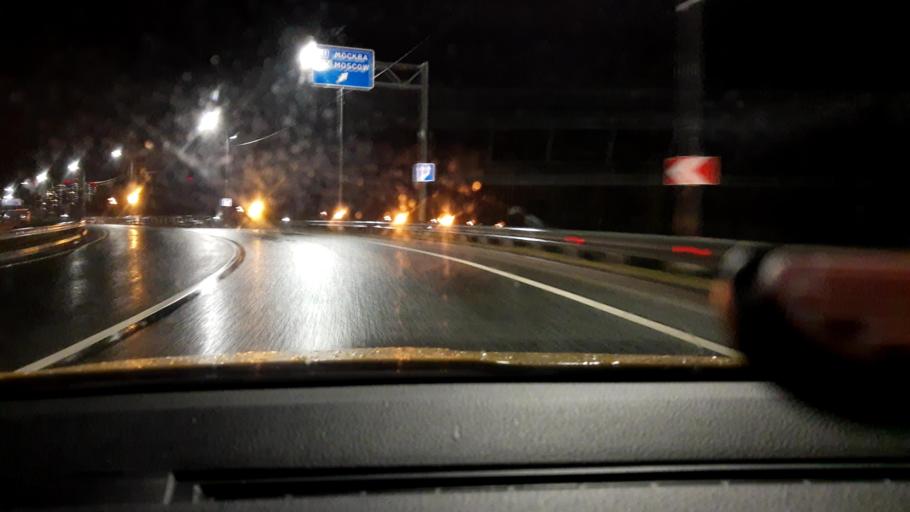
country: RU
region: Moskovskaya
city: Krasnoznamensk
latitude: 55.6103
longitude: 37.0547
